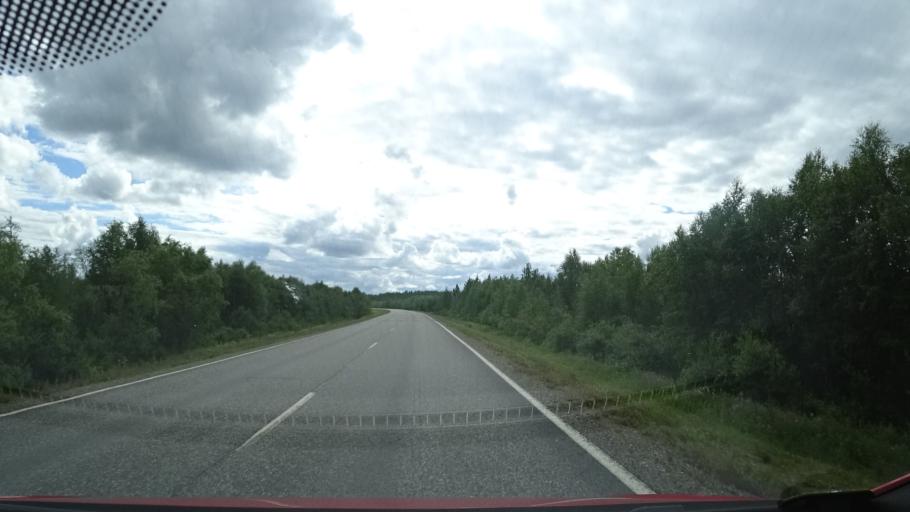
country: FI
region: Lapland
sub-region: Tunturi-Lappi
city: Kittilae
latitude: 67.5676
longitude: 24.9195
